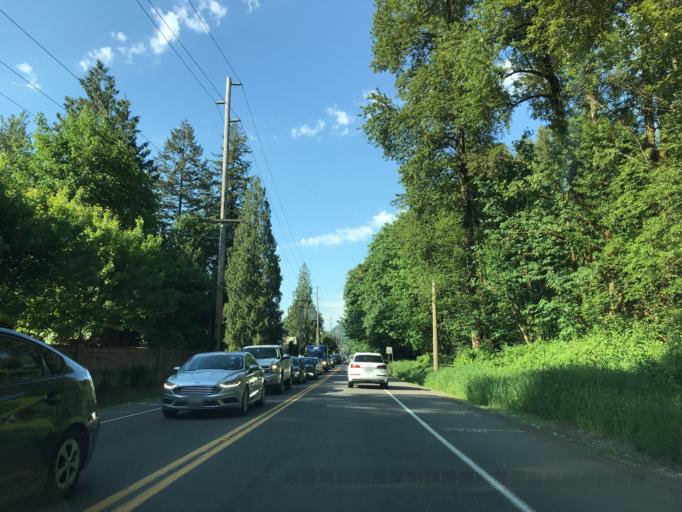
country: US
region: Washington
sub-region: King County
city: Mirrormont
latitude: 47.4857
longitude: -122.0266
